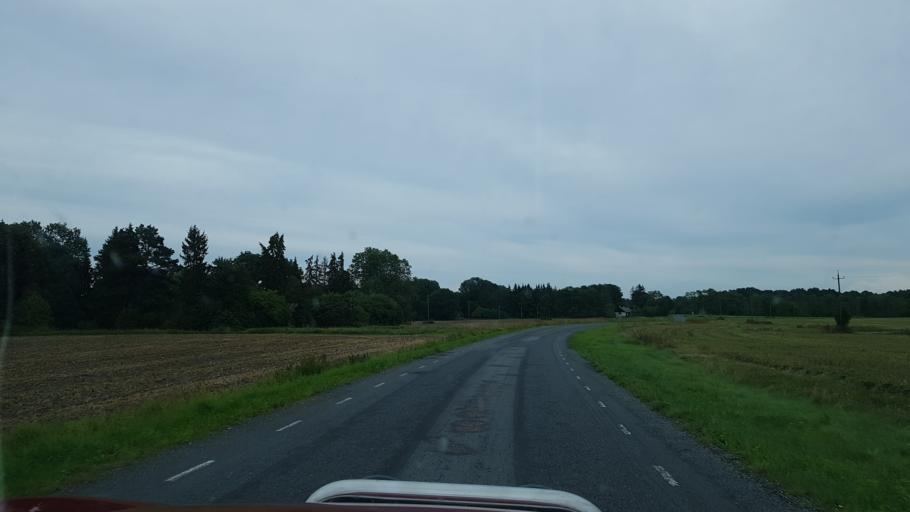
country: EE
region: Laeaene
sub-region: Lihula vald
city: Lihula
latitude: 58.8767
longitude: 23.8618
